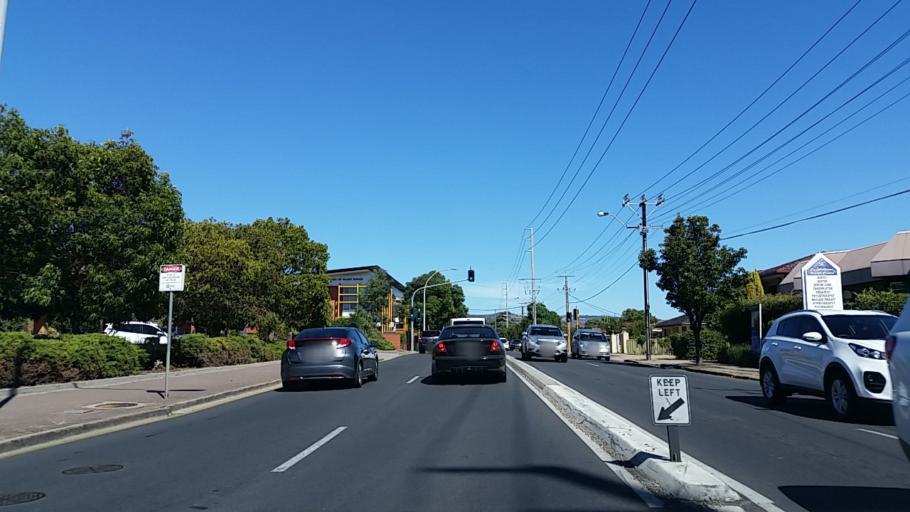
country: AU
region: South Australia
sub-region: Campbelltown
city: Campbelltown
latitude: -34.8816
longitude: 138.6737
